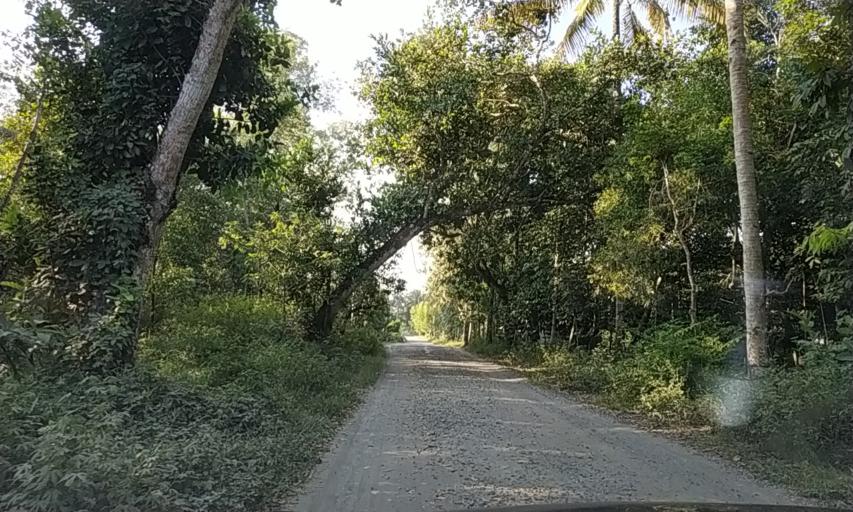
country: ID
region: Central Java
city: Gombong
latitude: -7.7604
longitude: 109.5193
